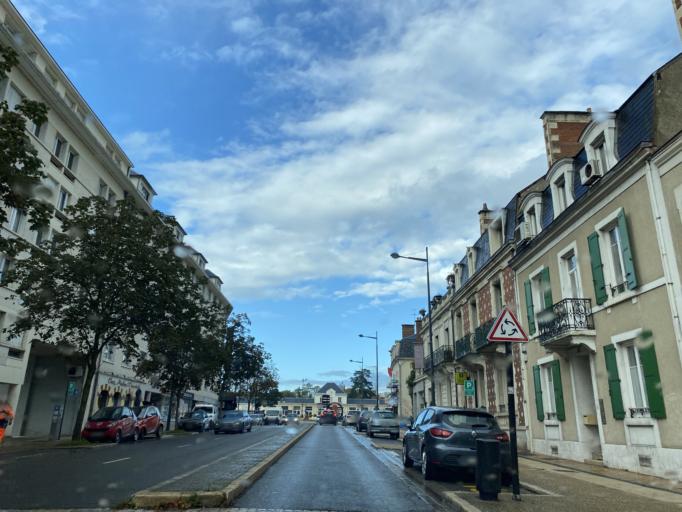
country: FR
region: Centre
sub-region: Departement du Cher
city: Bourges
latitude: 47.0926
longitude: 2.3939
